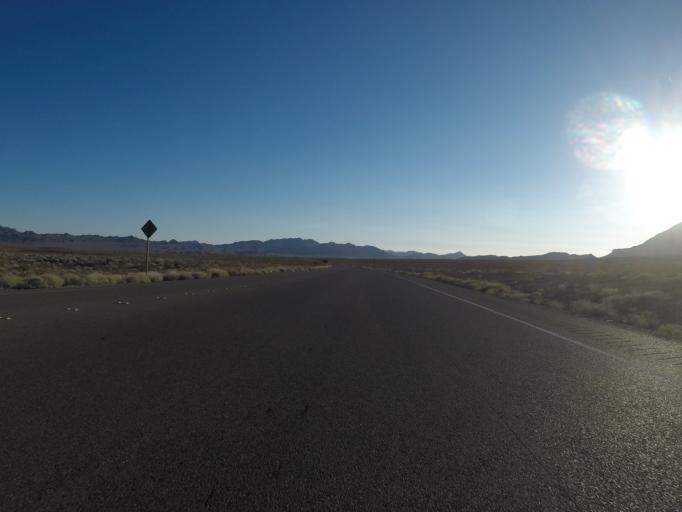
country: US
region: Nevada
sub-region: Clark County
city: Moapa Valley
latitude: 36.3340
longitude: -114.4923
